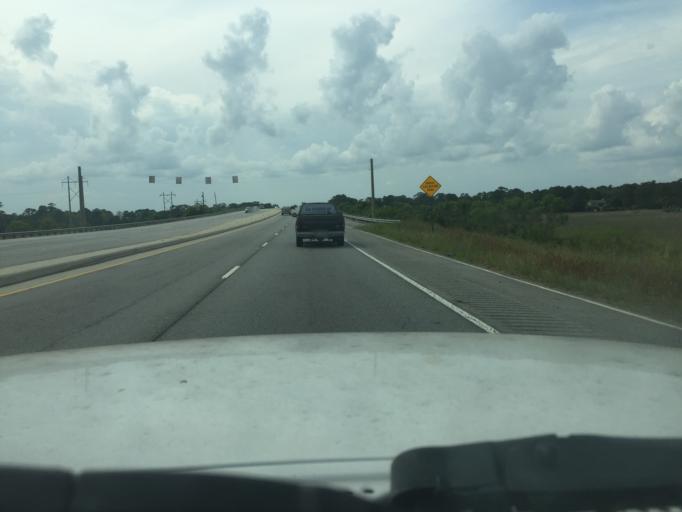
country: US
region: Georgia
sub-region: Chatham County
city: Wilmington Island
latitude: 32.0332
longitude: -80.9825
